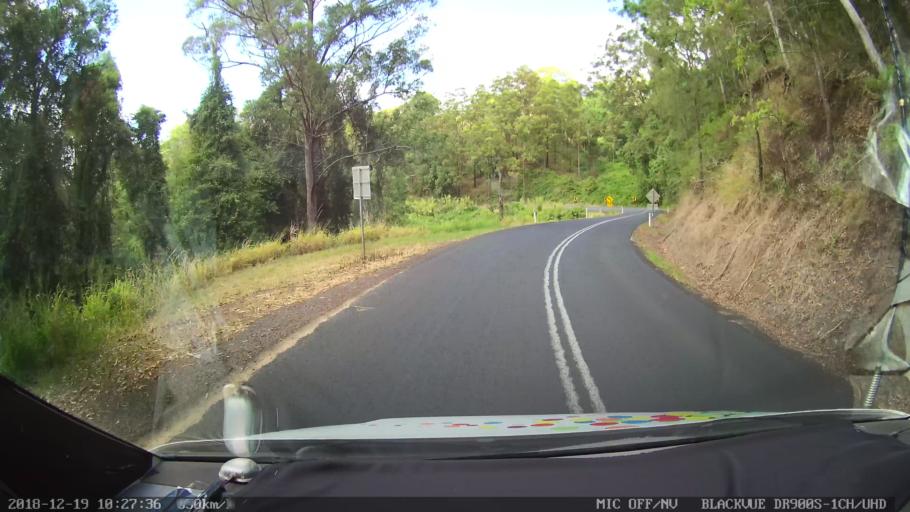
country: AU
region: New South Wales
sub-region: Lismore Municipality
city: Larnook
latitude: -28.5991
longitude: 153.0927
